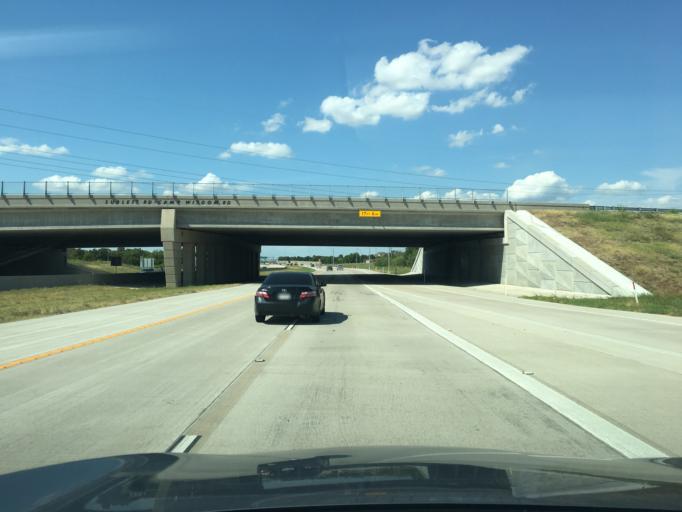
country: US
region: Texas
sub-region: Tarrant County
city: Arlington
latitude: 32.6476
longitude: -97.0620
